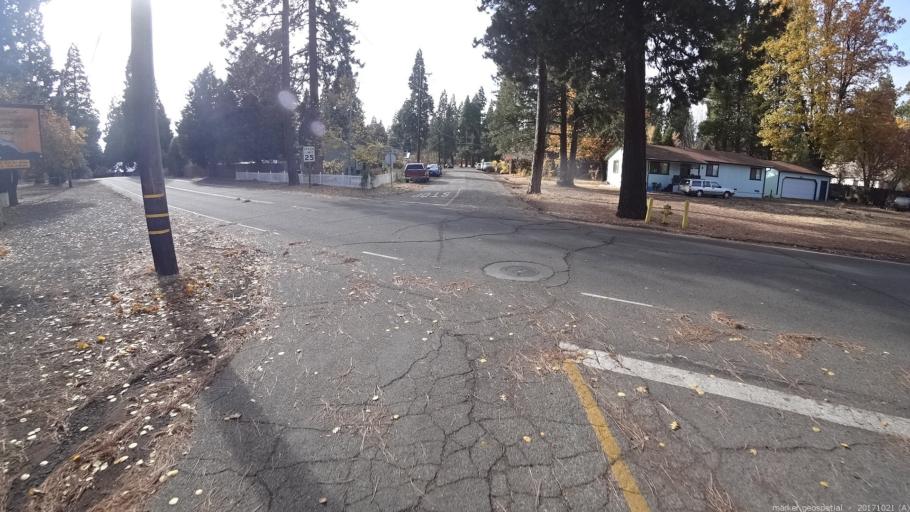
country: US
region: California
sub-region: Shasta County
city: Burney
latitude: 40.8790
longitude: -121.6725
